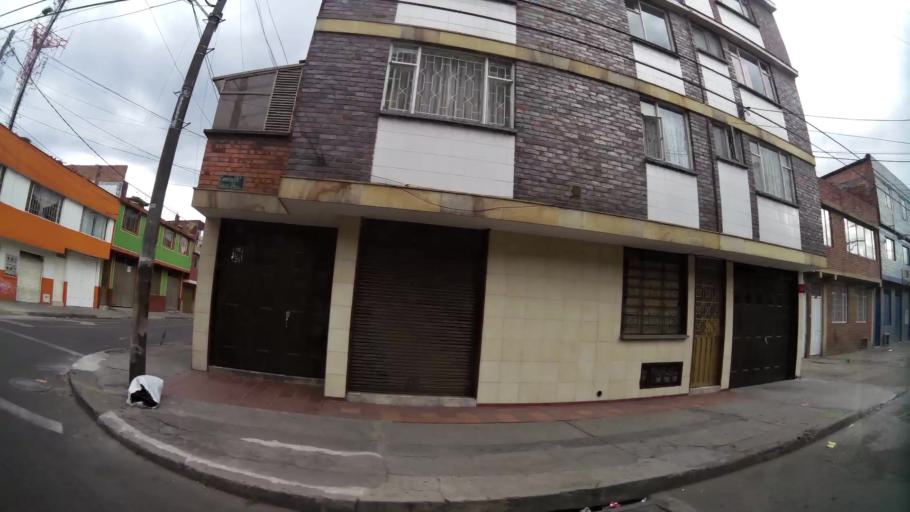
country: CO
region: Bogota D.C.
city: Bogota
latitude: 4.6125
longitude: -74.1370
